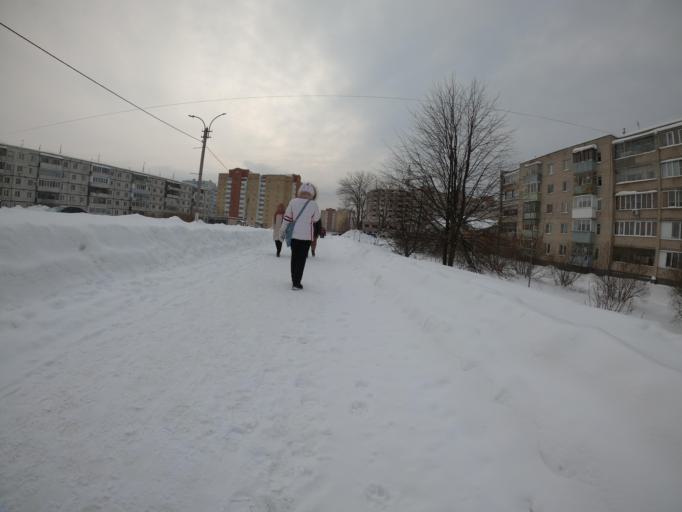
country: RU
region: Moskovskaya
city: Elektrogorsk
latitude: 55.8853
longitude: 38.7743
